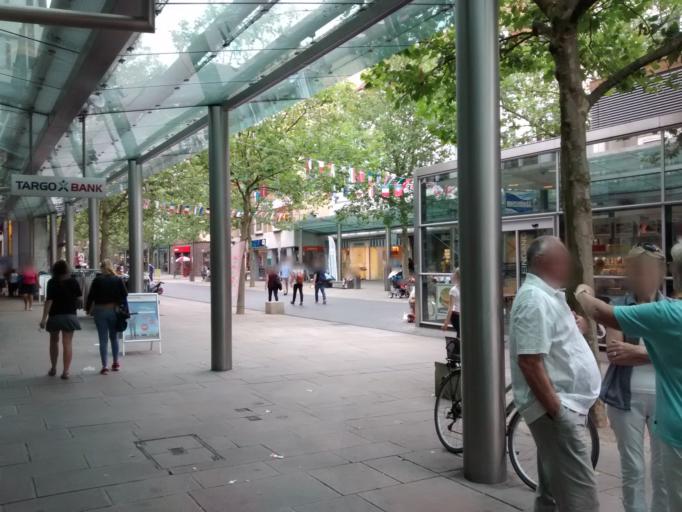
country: DE
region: Bremen
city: Bremerhaven
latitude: 53.5419
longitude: 8.5809
